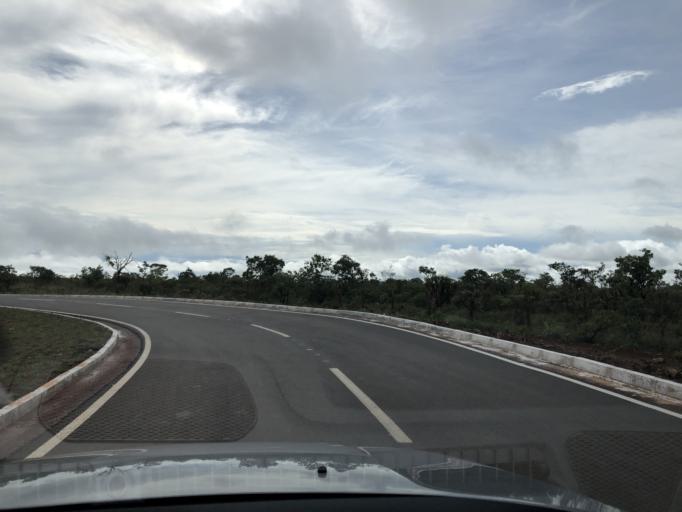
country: BR
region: Federal District
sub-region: Brasilia
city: Brasilia
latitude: -15.6235
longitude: -48.0671
